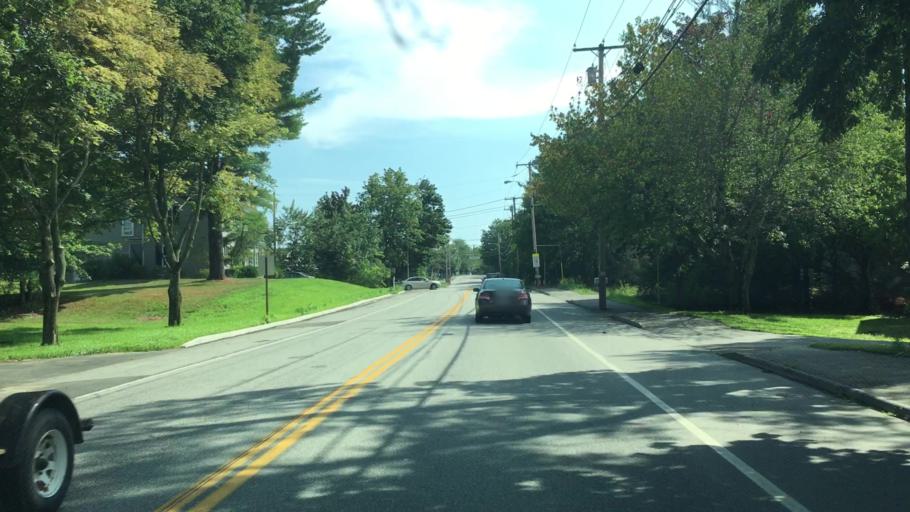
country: US
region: Maine
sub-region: Penobscot County
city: Hampden
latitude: 44.7432
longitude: -68.8380
